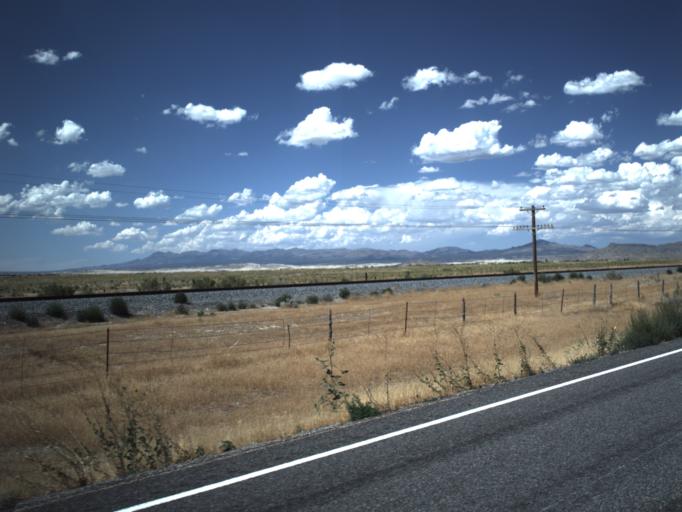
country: US
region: Utah
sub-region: Millard County
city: Delta
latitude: 39.5842
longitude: -112.3345
